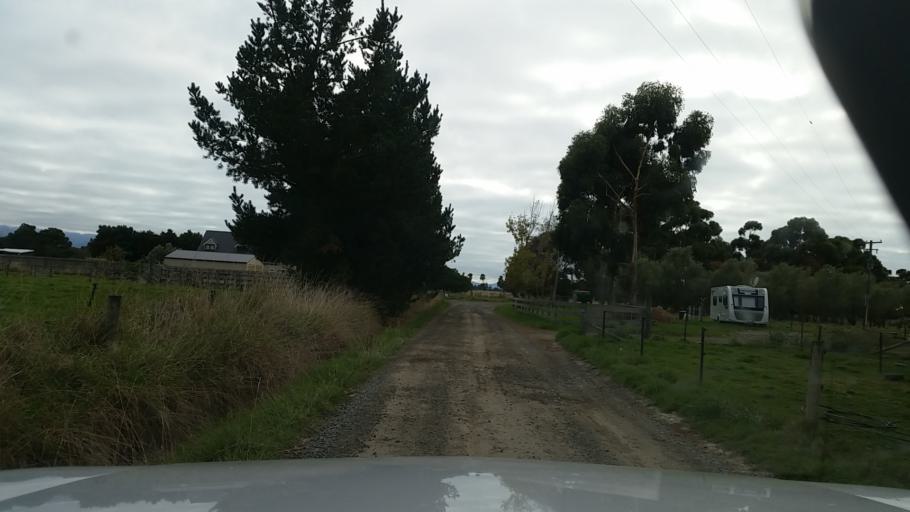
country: NZ
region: Marlborough
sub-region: Marlborough District
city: Blenheim
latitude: -41.5204
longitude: 174.0394
